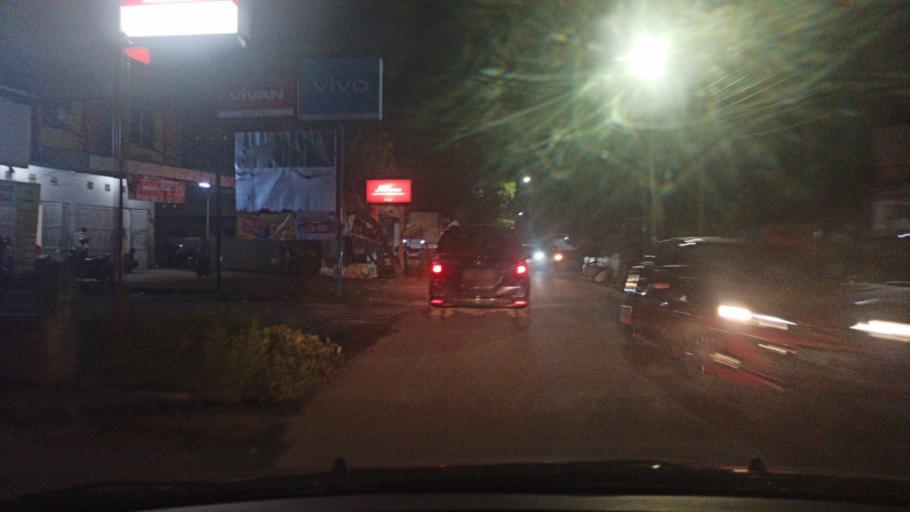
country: ID
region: South Sumatra
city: Palembang
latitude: -2.9222
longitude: 104.7811
